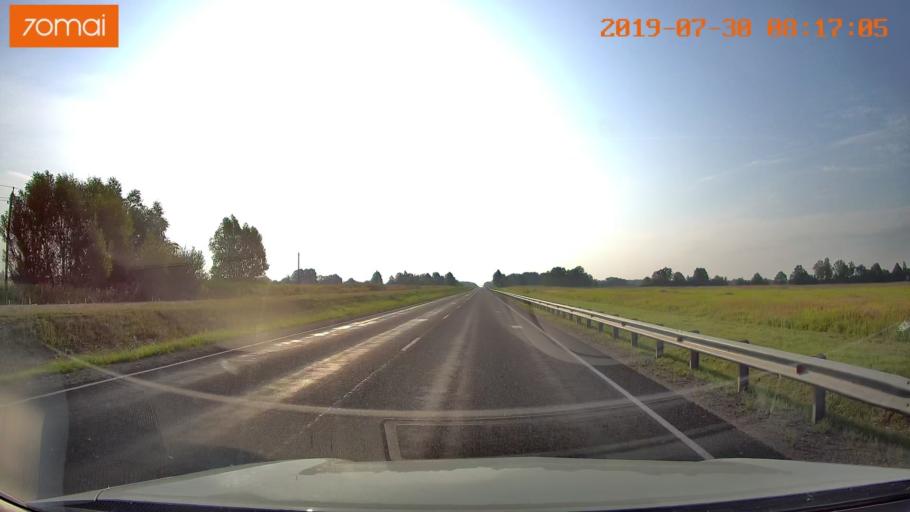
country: RU
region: Kaliningrad
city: Zheleznodorozhnyy
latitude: 54.6375
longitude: 21.4280
